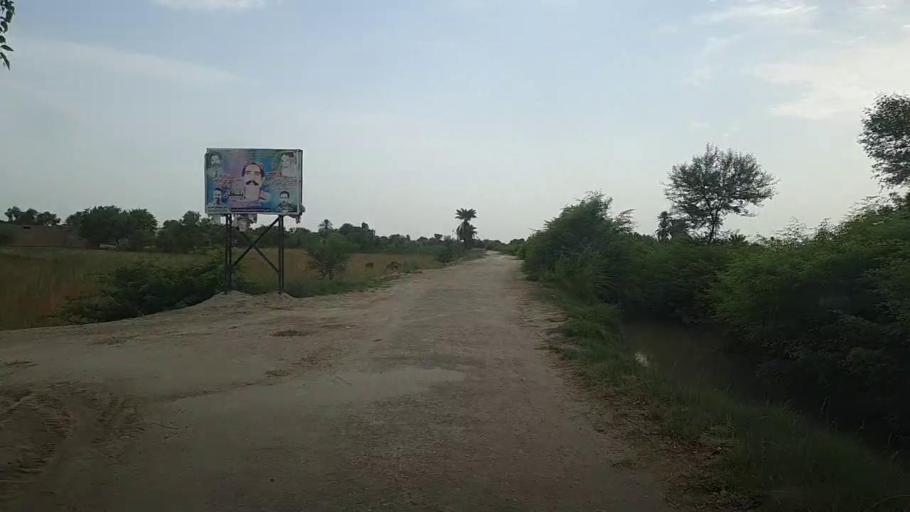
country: PK
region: Sindh
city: Karaundi
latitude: 26.9450
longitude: 68.4095
